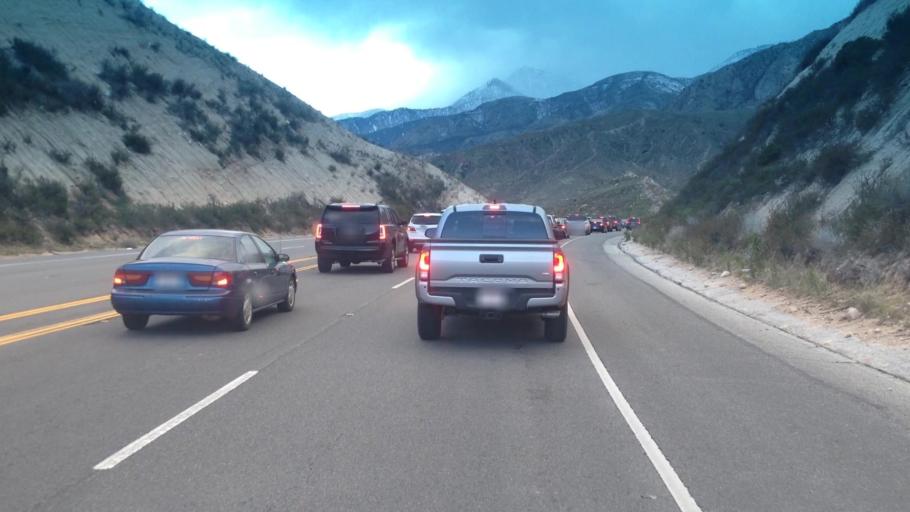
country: US
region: California
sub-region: San Bernardino County
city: Oak Hills
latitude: 34.3137
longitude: -117.4669
